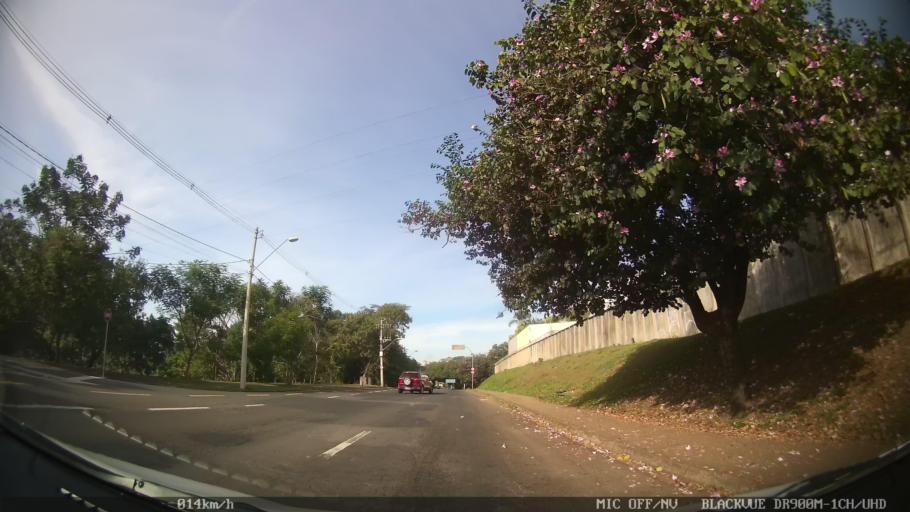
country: BR
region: Sao Paulo
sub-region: Piracicaba
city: Piracicaba
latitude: -22.7308
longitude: -47.6726
